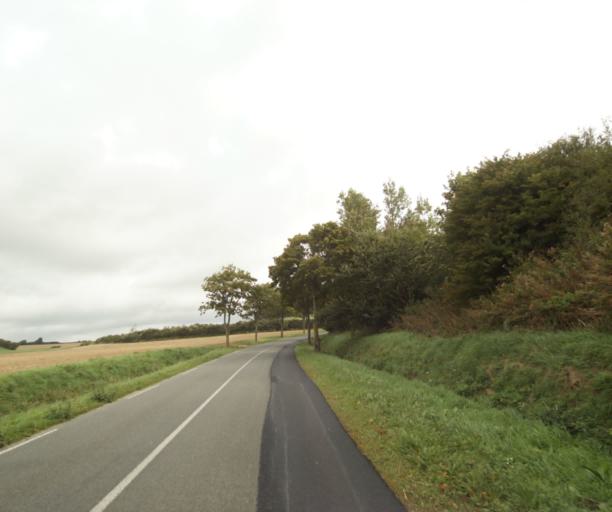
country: FR
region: Nord-Pas-de-Calais
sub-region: Departement du Pas-de-Calais
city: Etaples
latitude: 50.5212
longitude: 1.6730
